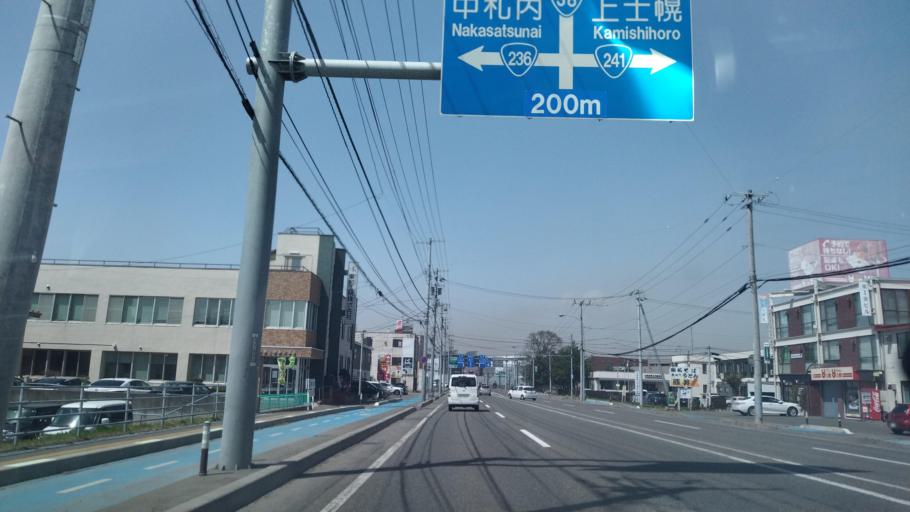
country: JP
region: Hokkaido
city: Obihiro
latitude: 42.9312
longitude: 143.2068
